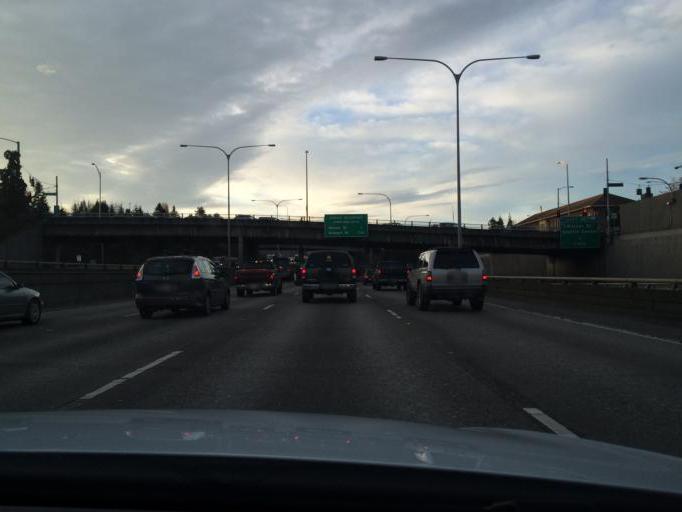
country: US
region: Washington
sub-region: King County
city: Seattle
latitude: 47.6440
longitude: -122.3228
